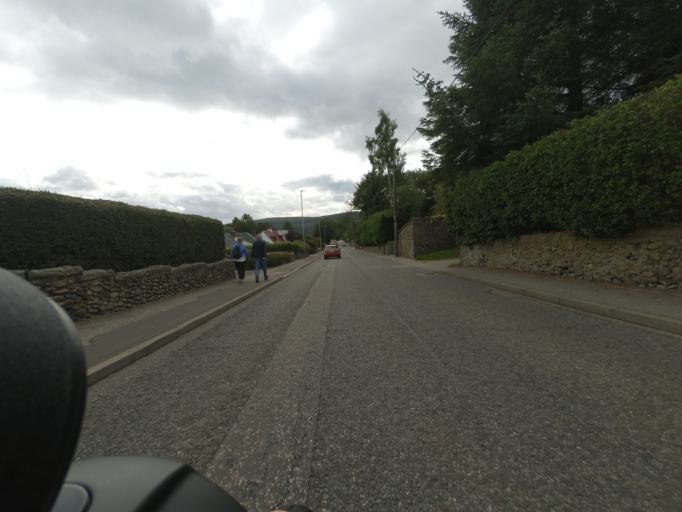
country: GB
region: Scotland
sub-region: Aberdeenshire
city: Banchory
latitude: 57.0576
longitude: -2.4922
